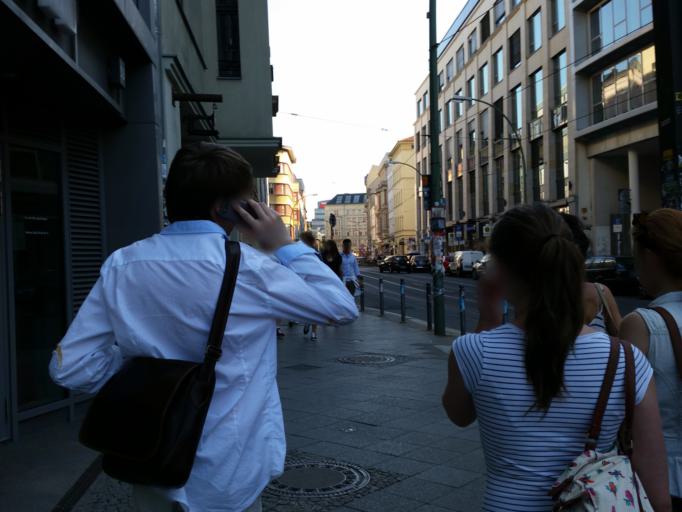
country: DE
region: Berlin
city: Mitte
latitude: 52.5258
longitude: 13.4038
